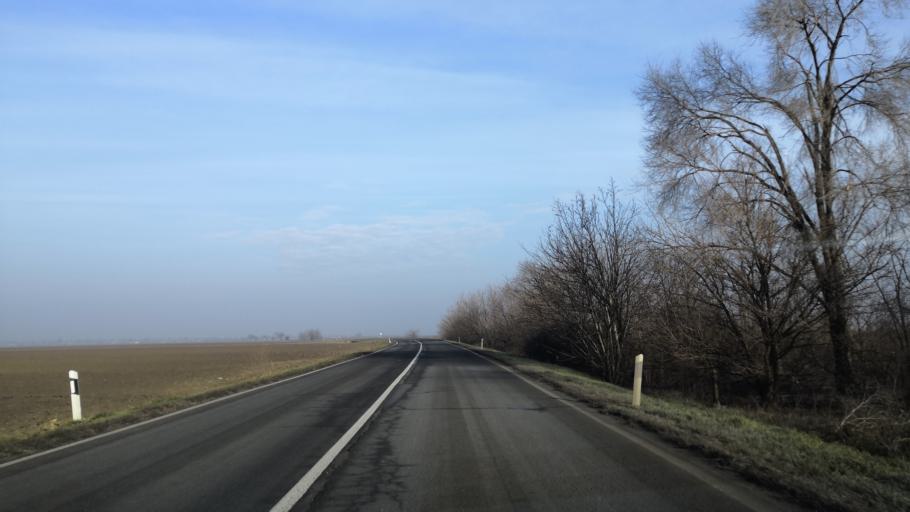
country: RS
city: Rumenka
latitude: 45.3227
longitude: 19.7374
